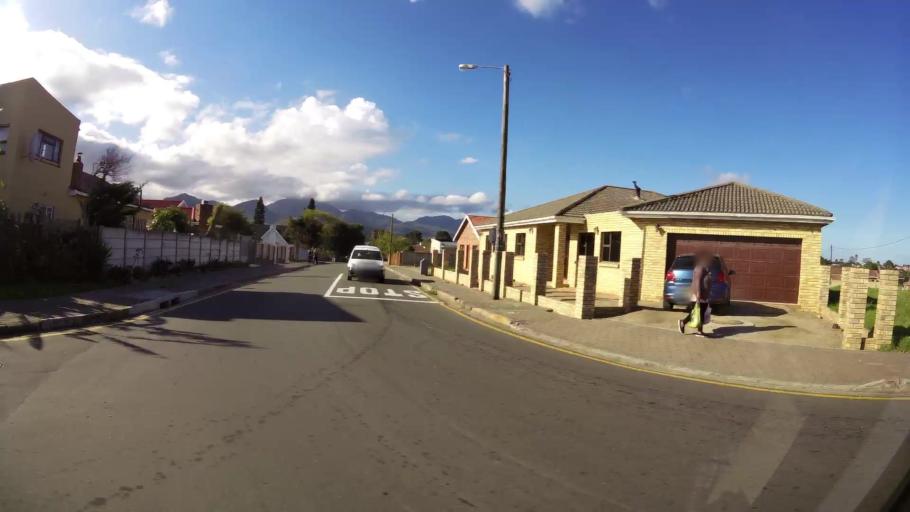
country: ZA
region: Western Cape
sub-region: Eden District Municipality
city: George
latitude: -33.9700
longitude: 22.4824
